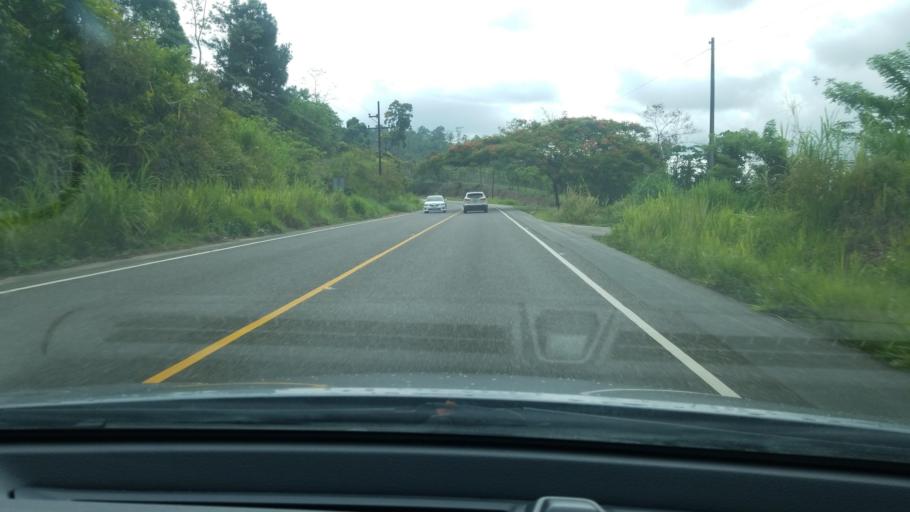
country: HN
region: Cortes
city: Potrerillos
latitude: 15.6100
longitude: -88.2883
